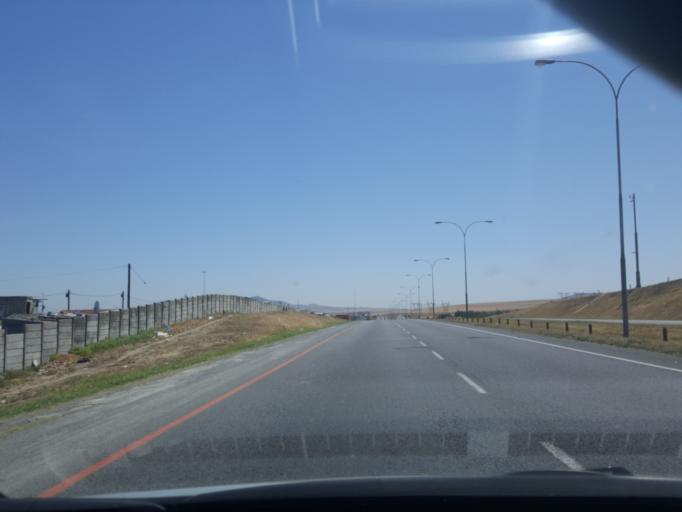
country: ZA
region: Western Cape
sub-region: City of Cape Town
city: Sunset Beach
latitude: -33.8236
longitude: 18.5421
